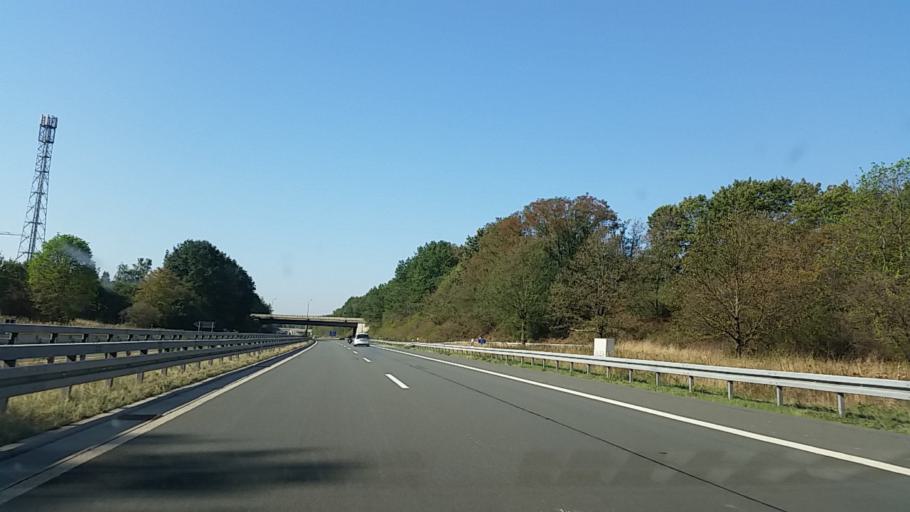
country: DE
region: North Rhine-Westphalia
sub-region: Regierungsbezirk Dusseldorf
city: Langenfeld
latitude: 51.0944
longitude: 6.9535
